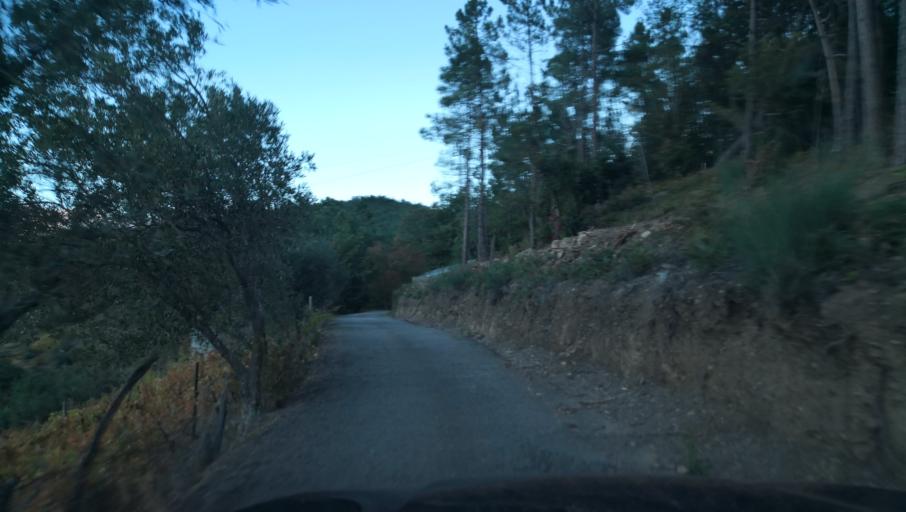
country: PT
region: Vila Real
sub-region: Santa Marta de Penaguiao
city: Santa Marta de Penaguiao
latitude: 41.2646
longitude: -7.8287
